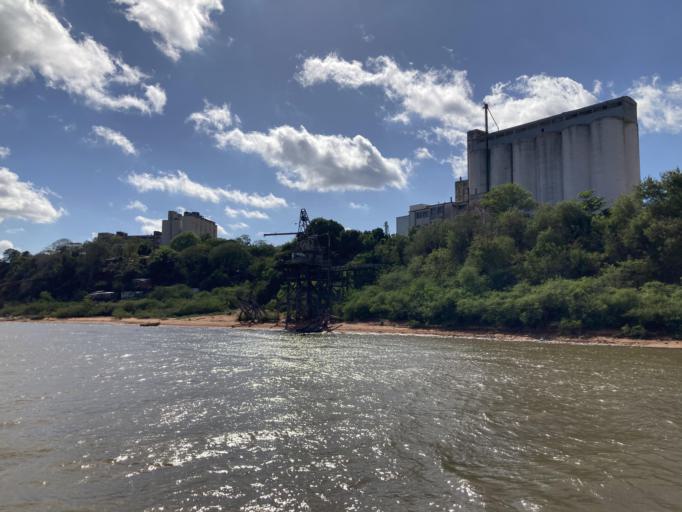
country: PY
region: Presidente Hayes
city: Nanawa
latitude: -25.2871
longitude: -57.6697
